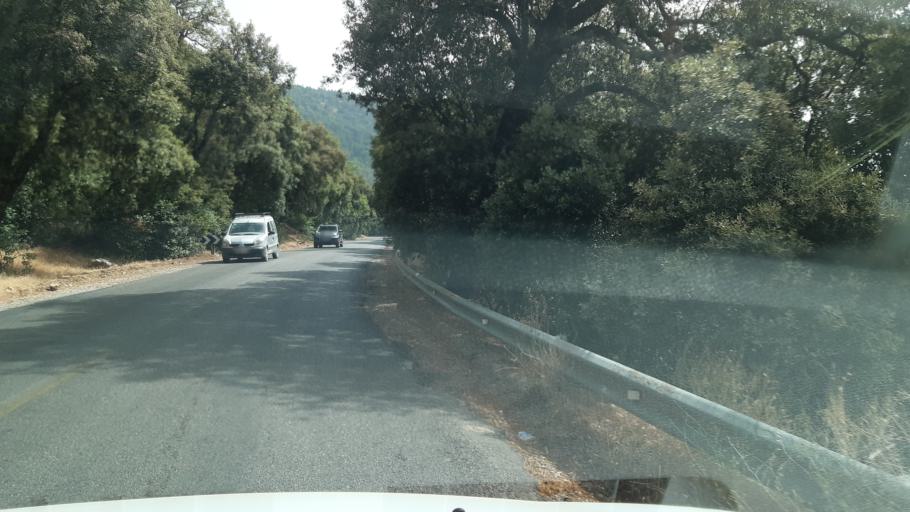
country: MA
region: Meknes-Tafilalet
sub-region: Ifrane
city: Azrou
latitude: 33.4317
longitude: -5.1881
